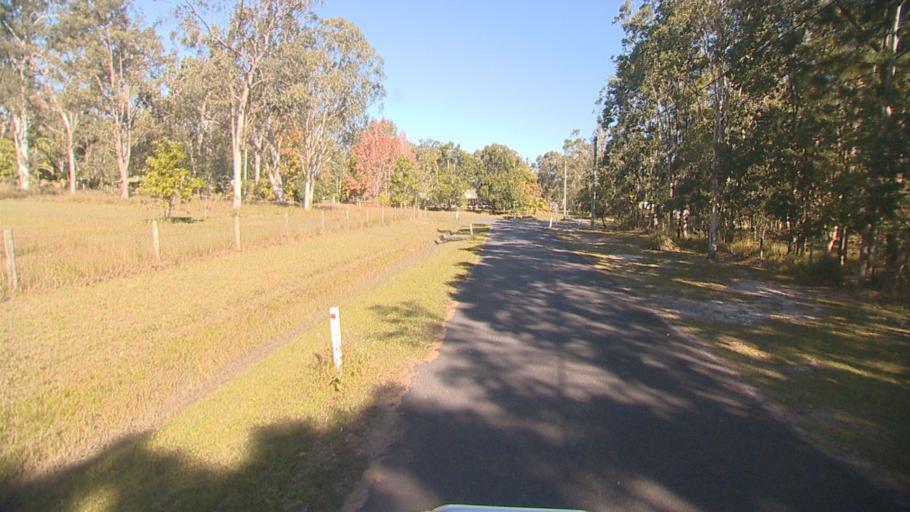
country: AU
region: Queensland
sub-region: Logan
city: Logan Reserve
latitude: -27.7209
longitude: 153.0693
